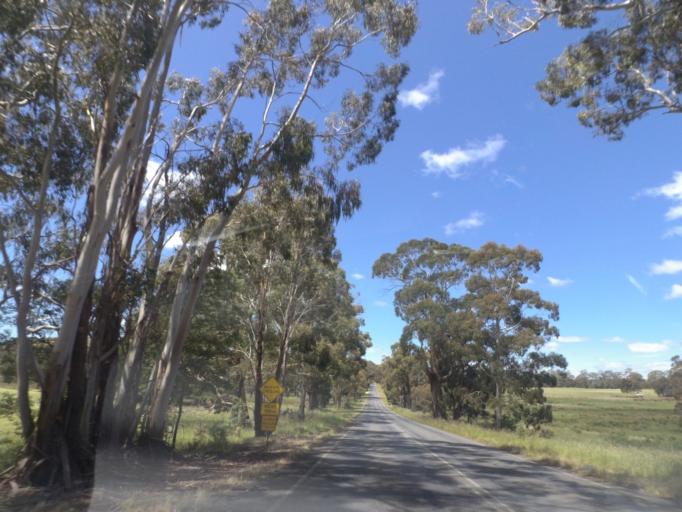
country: AU
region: Victoria
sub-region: Mount Alexander
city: Castlemaine
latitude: -37.3180
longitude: 144.2131
